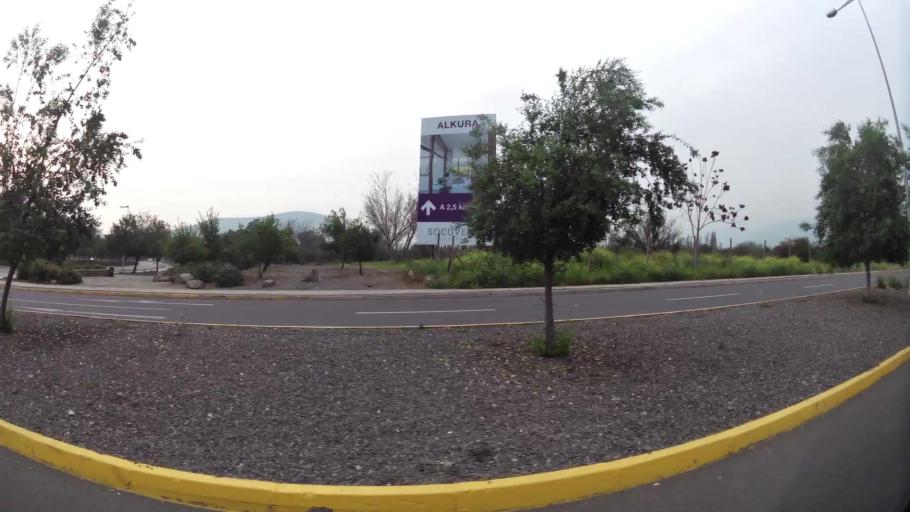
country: CL
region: Santiago Metropolitan
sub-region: Provincia de Chacabuco
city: Chicureo Abajo
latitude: -33.2649
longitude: -70.6236
